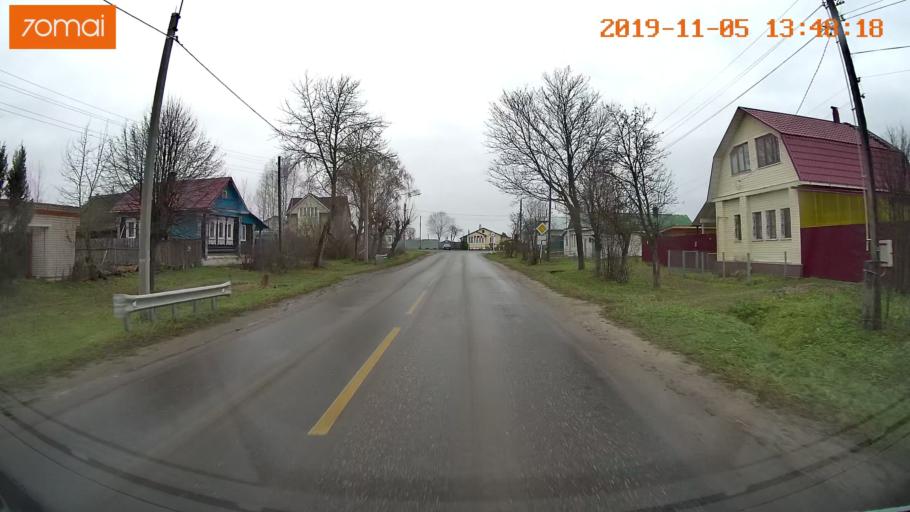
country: RU
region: Ivanovo
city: Shuya
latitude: 57.0033
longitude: 41.4055
